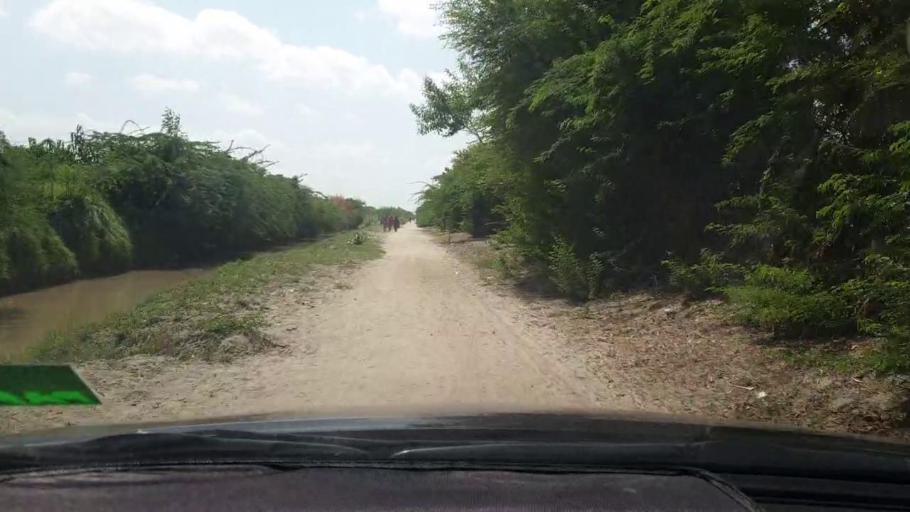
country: PK
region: Sindh
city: Tando Bago
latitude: 24.8742
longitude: 69.0709
